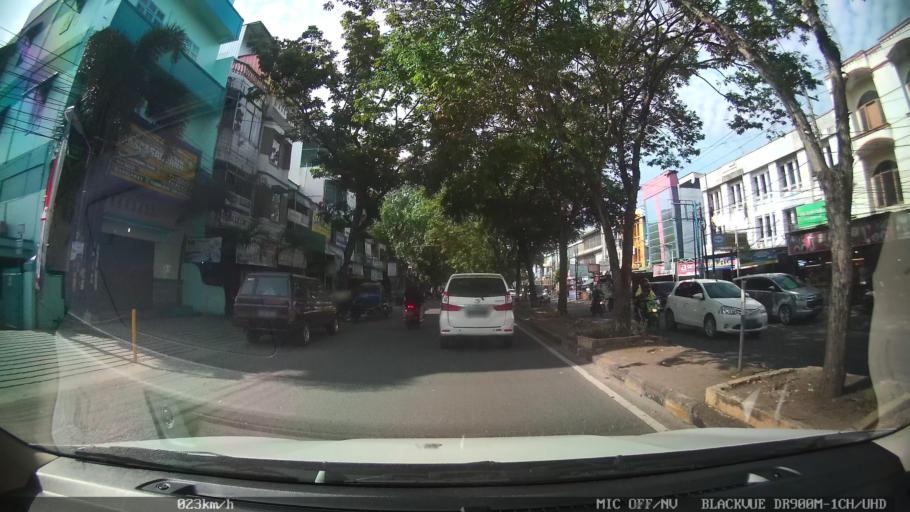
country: ID
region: North Sumatra
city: Medan
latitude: 3.5770
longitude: 98.6429
